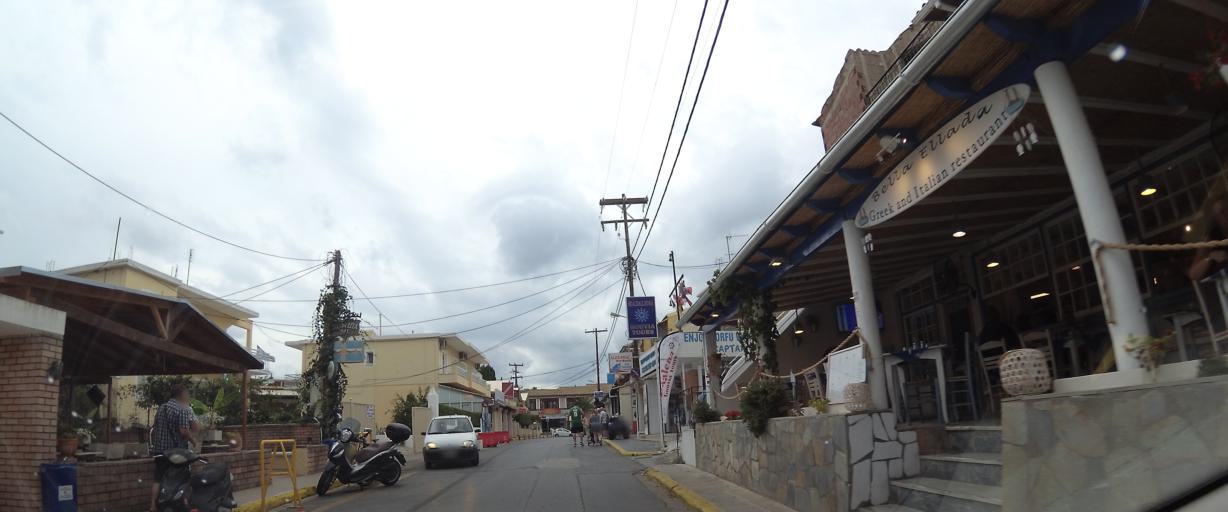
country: GR
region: Ionian Islands
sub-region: Nomos Kerkyras
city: Kontokali
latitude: 39.6527
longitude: 19.8433
